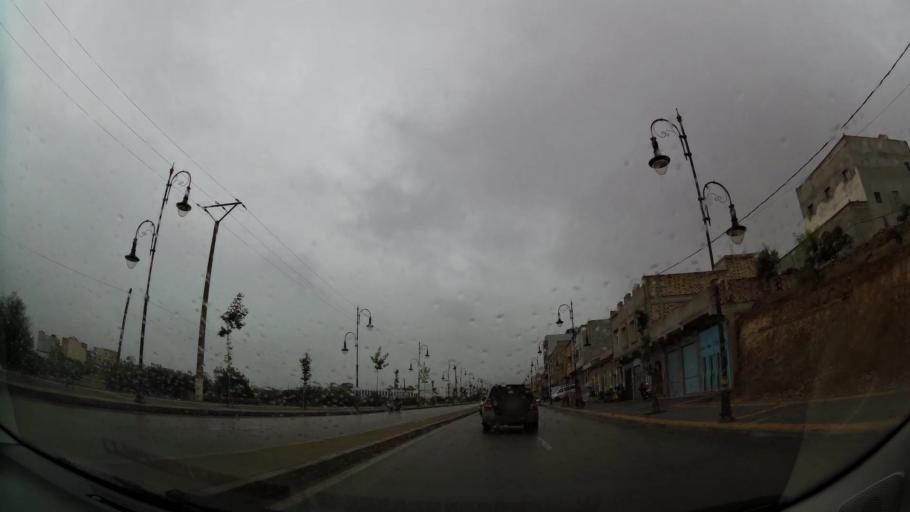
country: MA
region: Taza-Al Hoceima-Taounate
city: Imzourene
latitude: 35.1685
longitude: -3.8584
